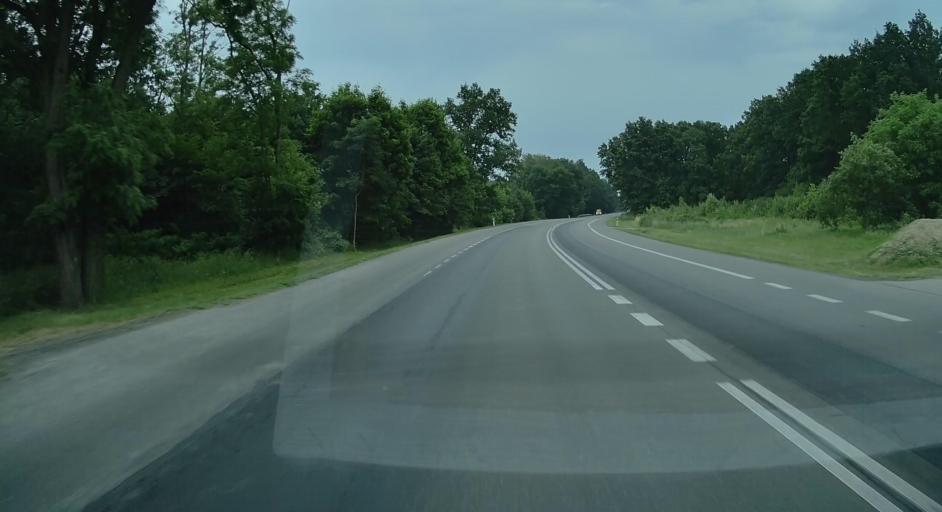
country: PL
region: Lublin Voivodeship
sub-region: Powiat lukowski
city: Trzebieszow
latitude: 52.0582
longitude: 22.6232
